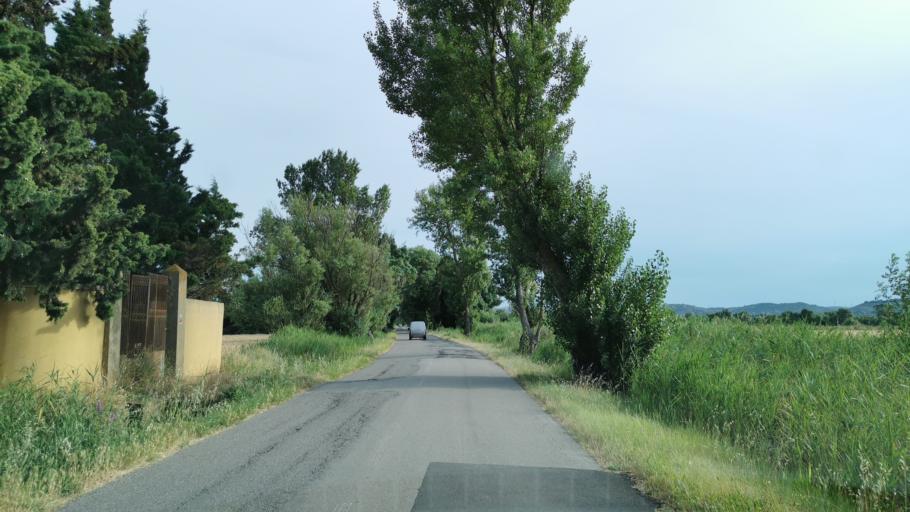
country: FR
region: Languedoc-Roussillon
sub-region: Departement de l'Aude
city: Narbonne
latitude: 43.1992
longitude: 2.9963
